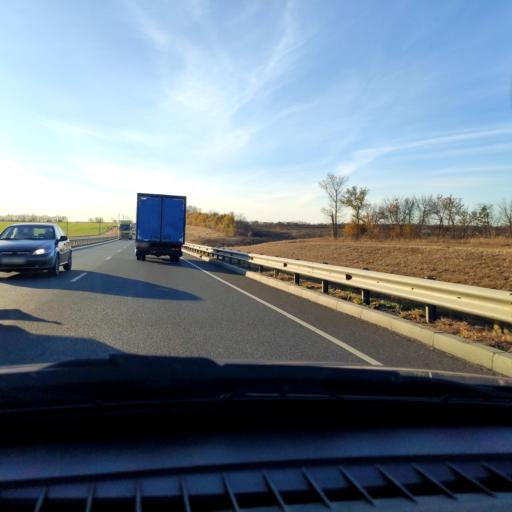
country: RU
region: Samara
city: Balasheyka
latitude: 53.1949
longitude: 48.0000
